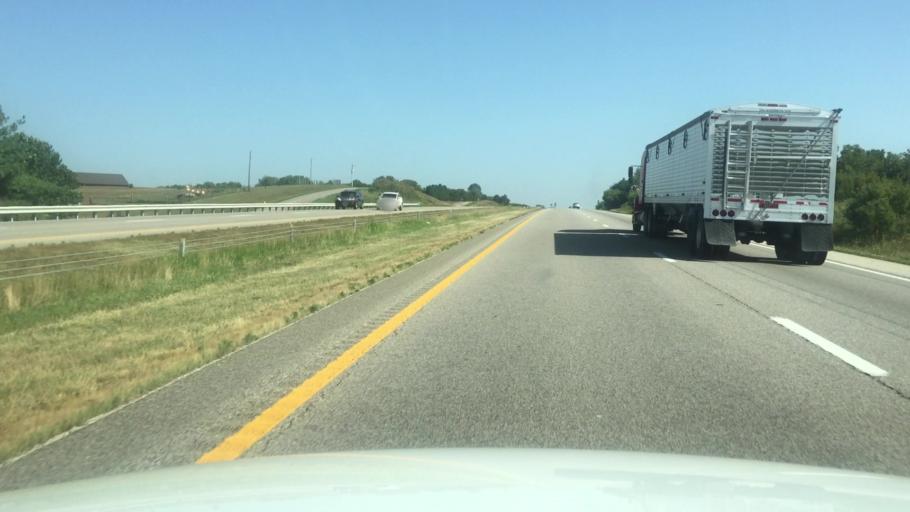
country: US
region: Kansas
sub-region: Doniphan County
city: Elwood
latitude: 39.5845
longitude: -94.7888
